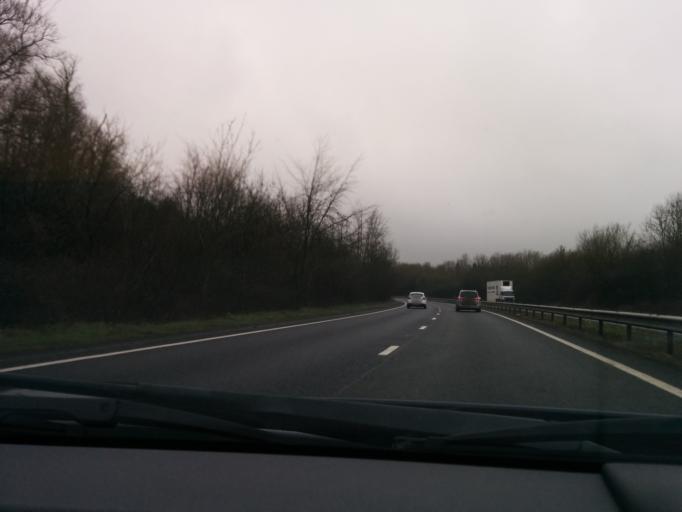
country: GB
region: England
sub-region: Hampshire
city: Highclere
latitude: 51.3324
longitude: -1.3465
